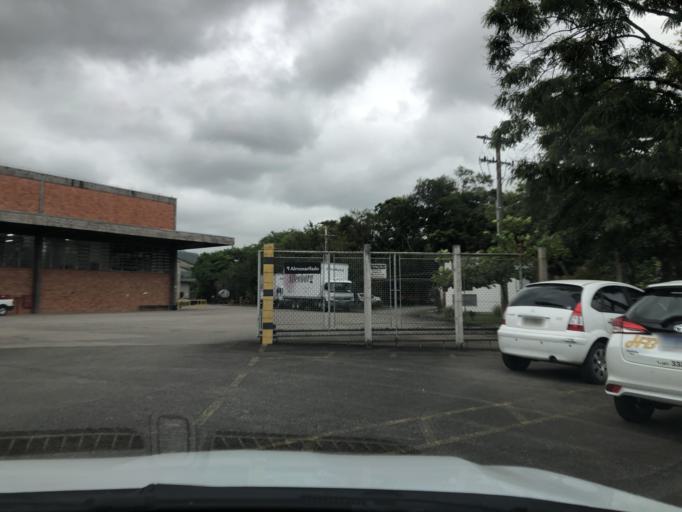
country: BR
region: Santa Catarina
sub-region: Indaial
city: Indaial
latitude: -26.8831
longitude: -49.1541
